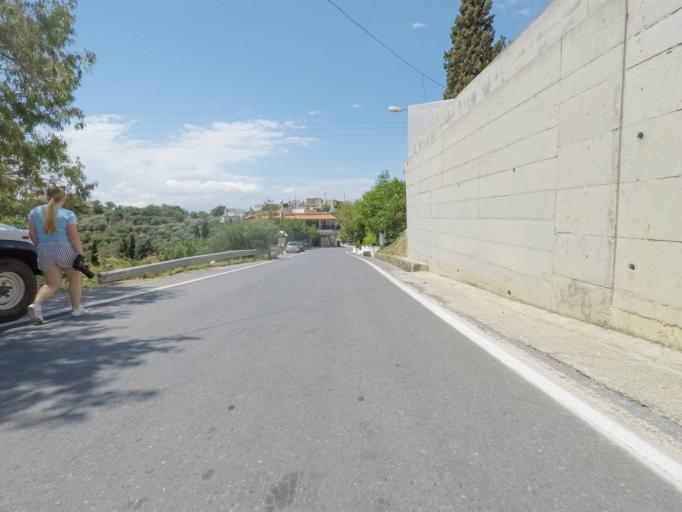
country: GR
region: Crete
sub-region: Nomos Irakleiou
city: Mokhos
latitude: 35.2194
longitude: 25.4607
